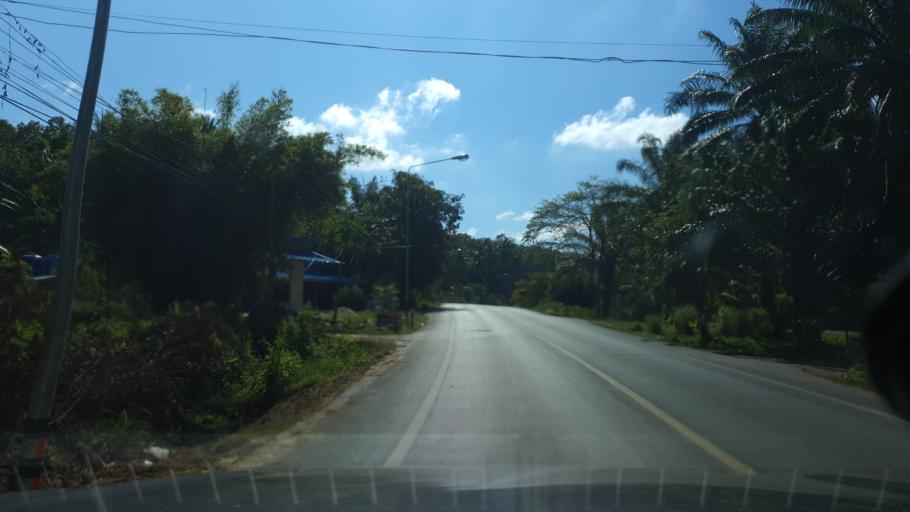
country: TH
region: Phangnga
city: Ban Ao Nang
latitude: 8.0714
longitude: 98.8077
